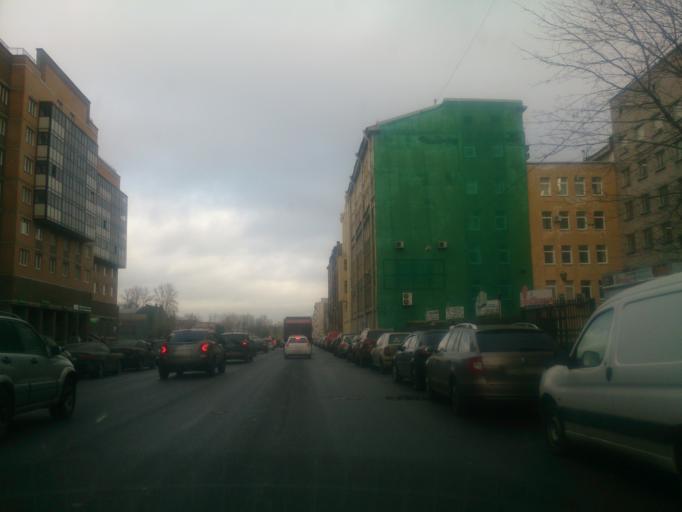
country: RU
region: St.-Petersburg
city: Admiralteisky
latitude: 59.9050
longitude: 30.2919
